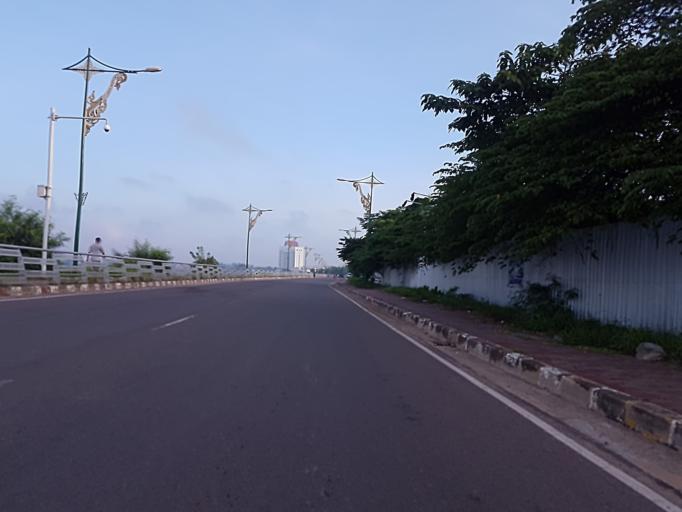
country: LA
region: Vientiane
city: Vientiane
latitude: 17.9451
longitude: 102.6160
